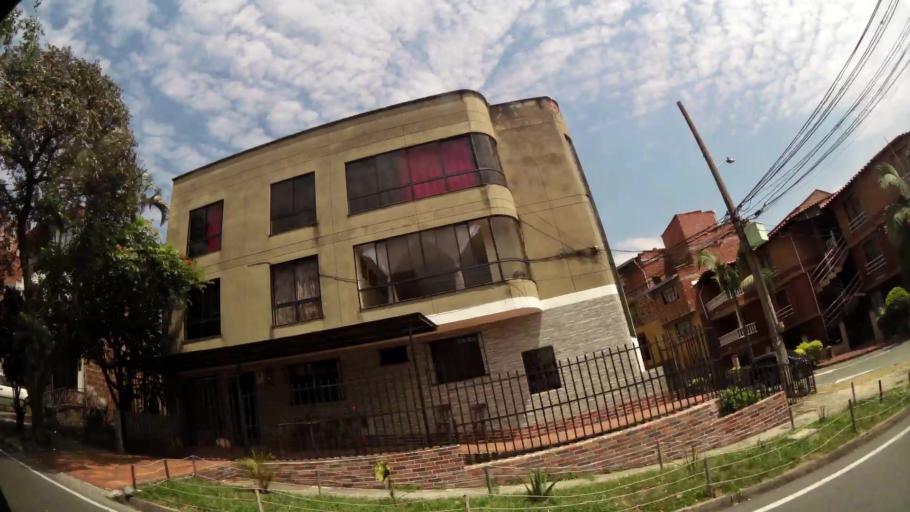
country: CO
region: Antioquia
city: Bello
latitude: 6.3140
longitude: -75.5652
